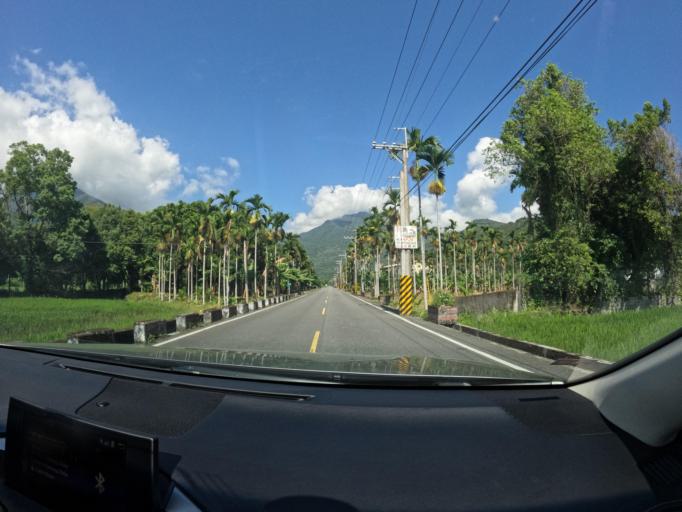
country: TW
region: Taiwan
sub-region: Hualien
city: Hualian
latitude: 23.5780
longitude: 121.3747
